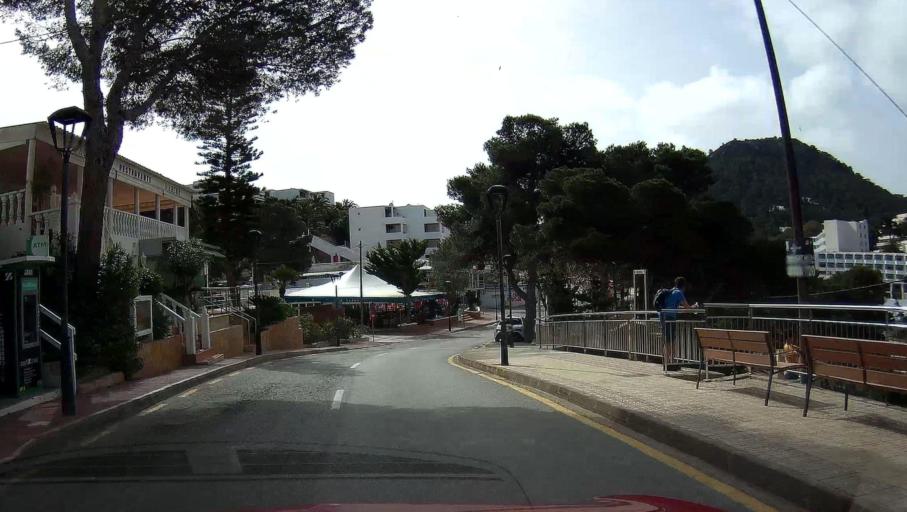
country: ES
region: Balearic Islands
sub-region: Illes Balears
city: Sant Joan de Labritja
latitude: 39.1108
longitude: 1.5172
